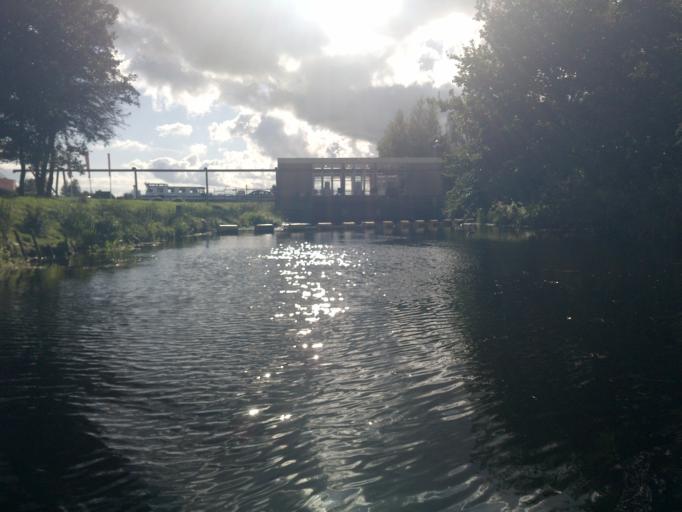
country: NL
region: Friesland
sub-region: Gemeente Tytsjerksteradiel
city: Garyp
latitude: 53.1358
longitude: 5.9542
